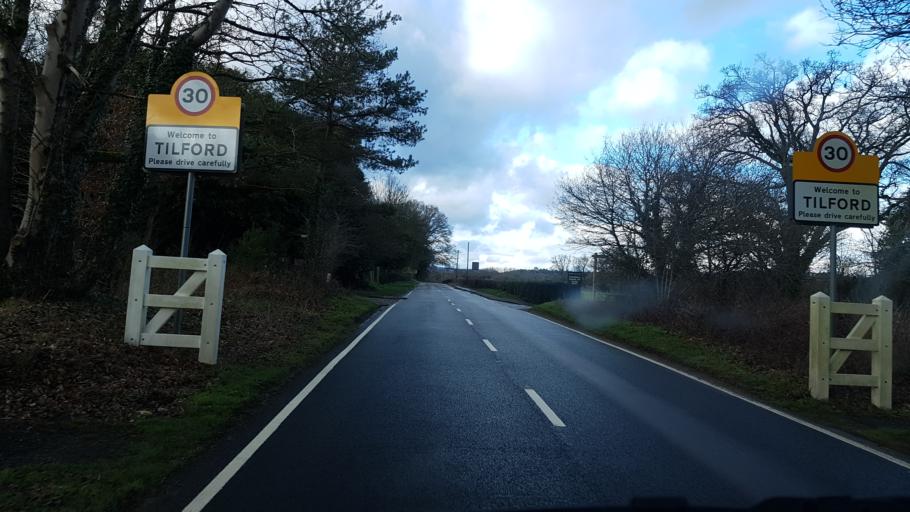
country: GB
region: England
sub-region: Surrey
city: Elstead
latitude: 51.1791
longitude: -0.7502
